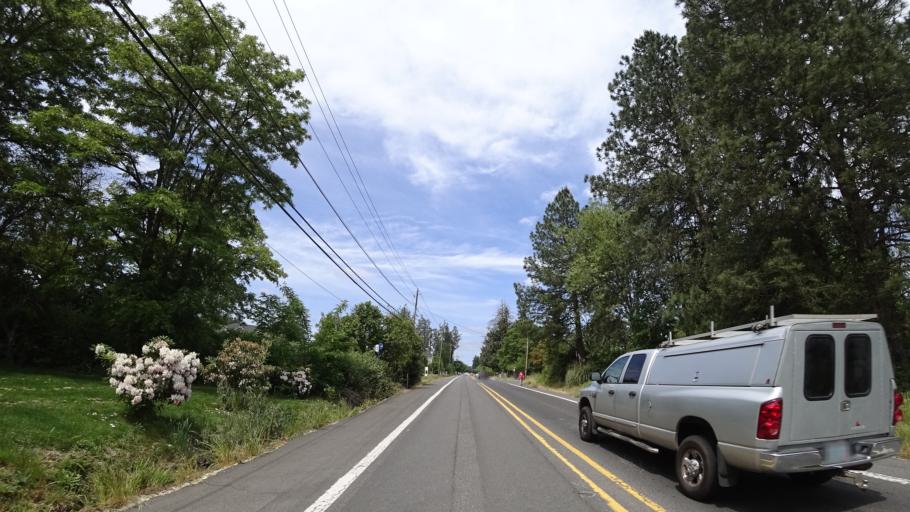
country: US
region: Oregon
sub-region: Washington County
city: Metzger
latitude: 45.4519
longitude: -122.7700
